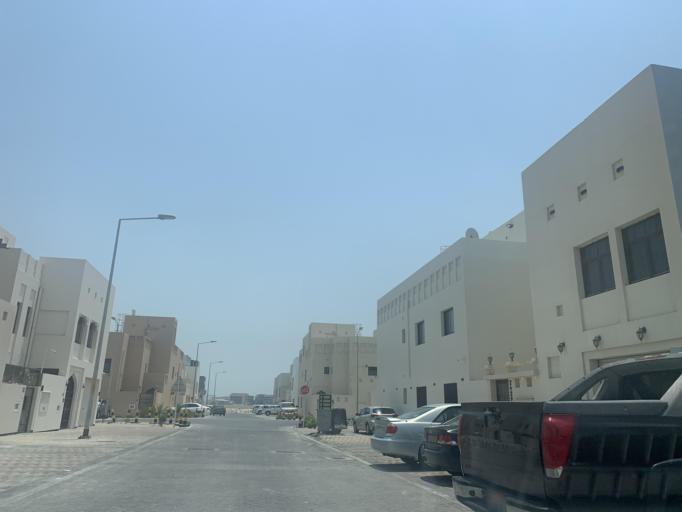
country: BH
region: Muharraq
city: Al Hadd
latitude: 26.2326
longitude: 50.6733
